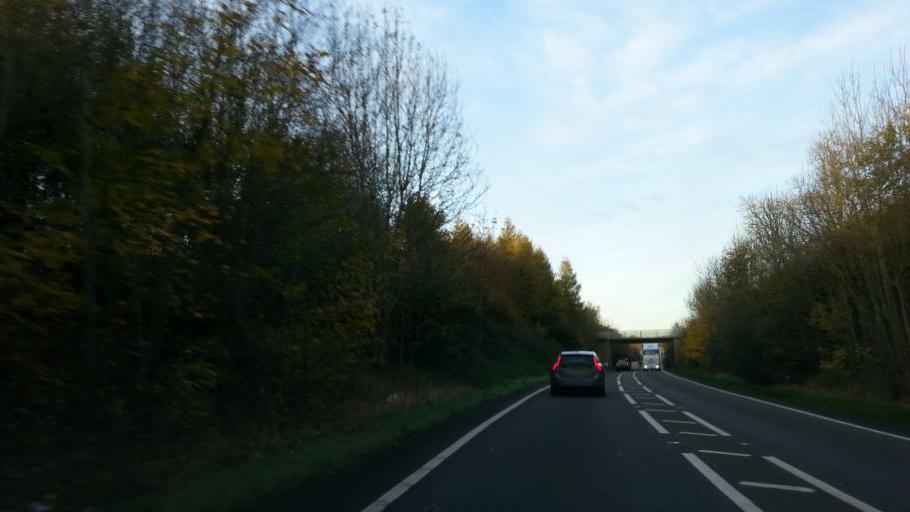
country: GB
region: England
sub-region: District of Rutland
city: South Luffenham
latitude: 52.5383
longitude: -0.5915
